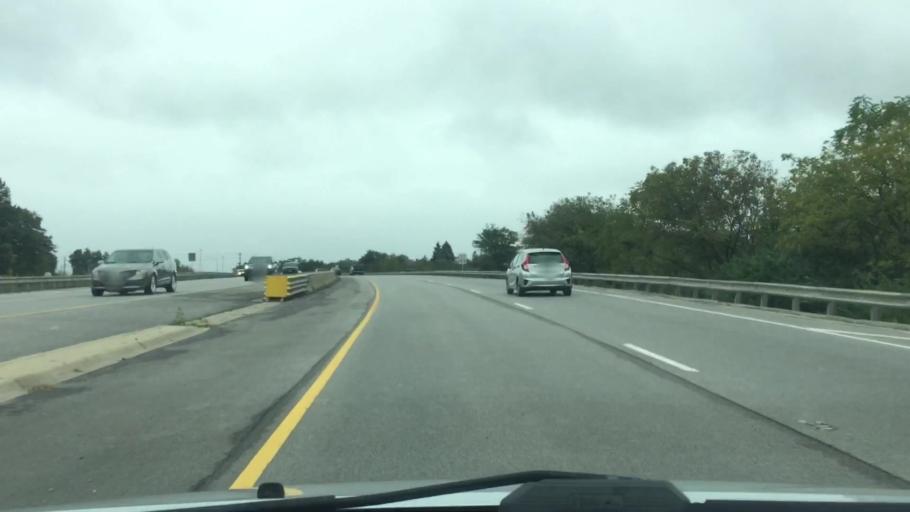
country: US
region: Illinois
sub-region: McHenry County
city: Crystal Lake
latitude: 42.2329
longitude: -88.2876
